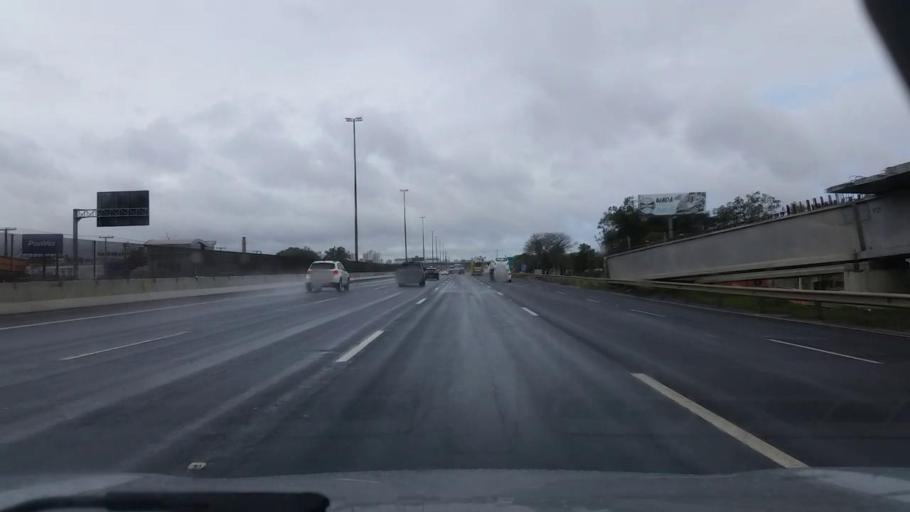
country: BR
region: Rio Grande do Sul
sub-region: Porto Alegre
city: Porto Alegre
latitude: -29.9901
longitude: -51.2042
